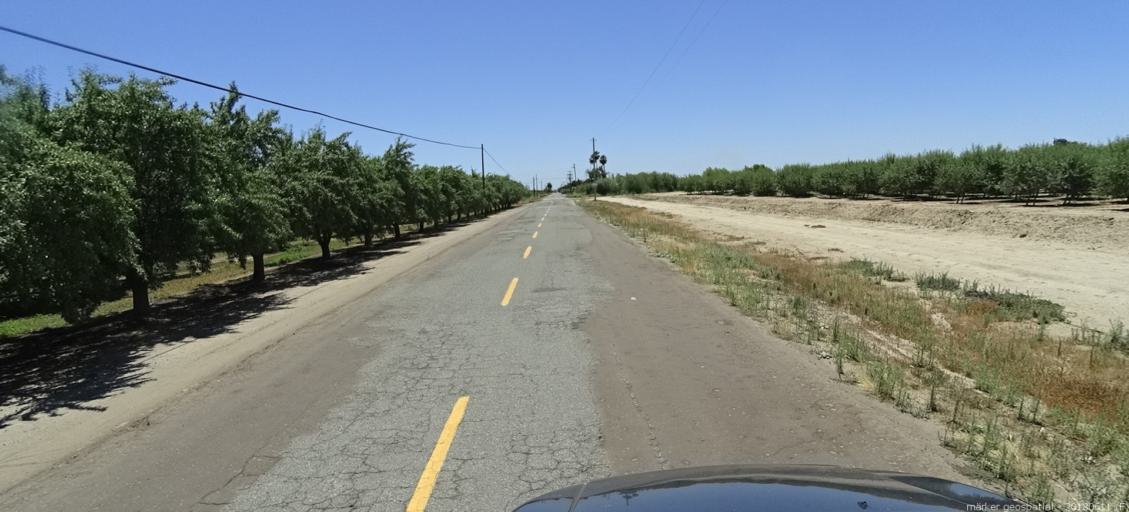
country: US
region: California
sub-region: Madera County
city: Fairmead
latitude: 37.0273
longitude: -120.1841
